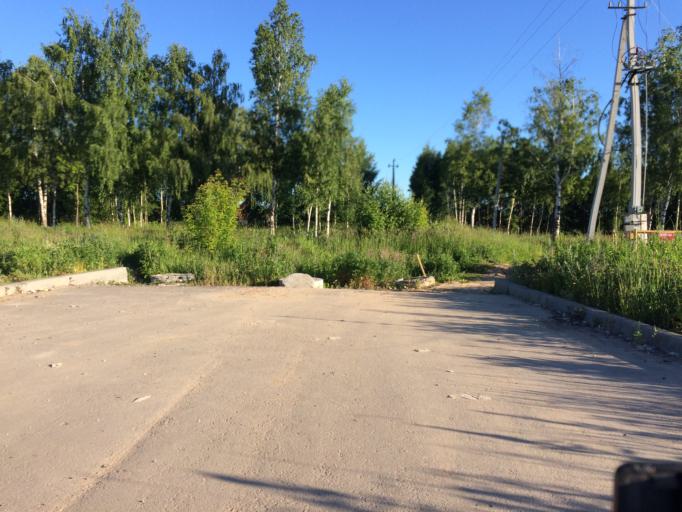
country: RU
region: Mariy-El
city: Medvedevo
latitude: 56.6501
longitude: 47.8332
